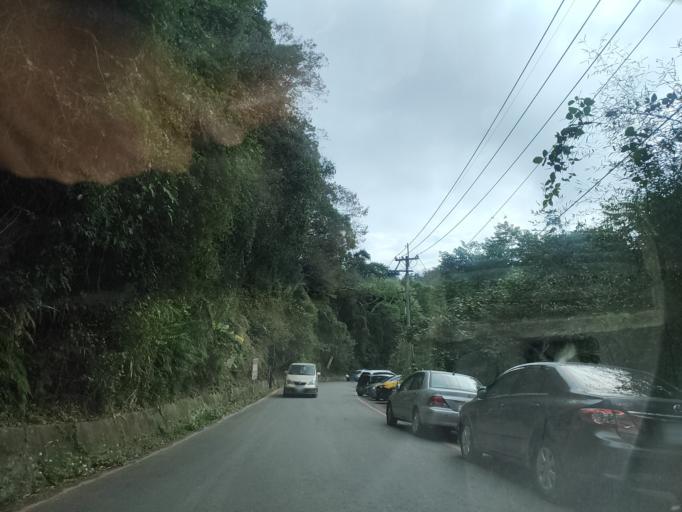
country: TW
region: Taiwan
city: Fengyuan
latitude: 24.3574
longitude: 120.7739
